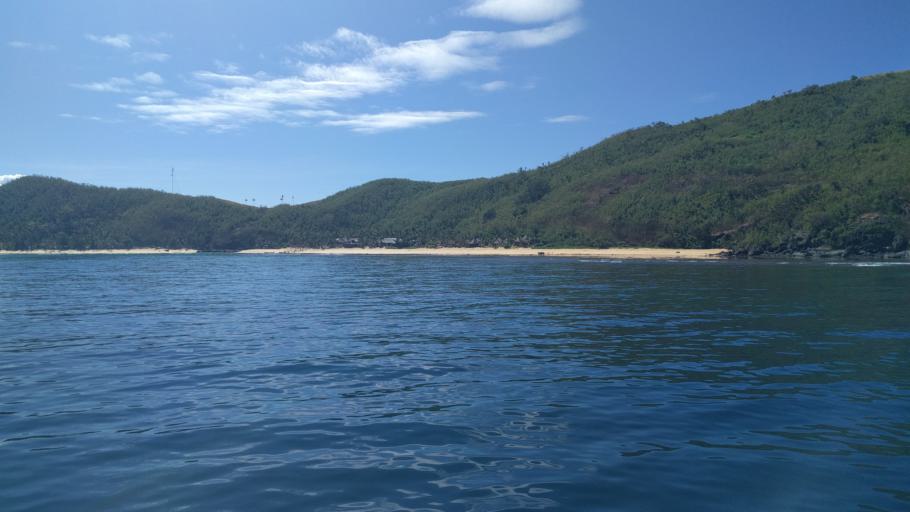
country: FJ
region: Western
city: Lautoka
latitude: -17.2797
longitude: 177.1032
